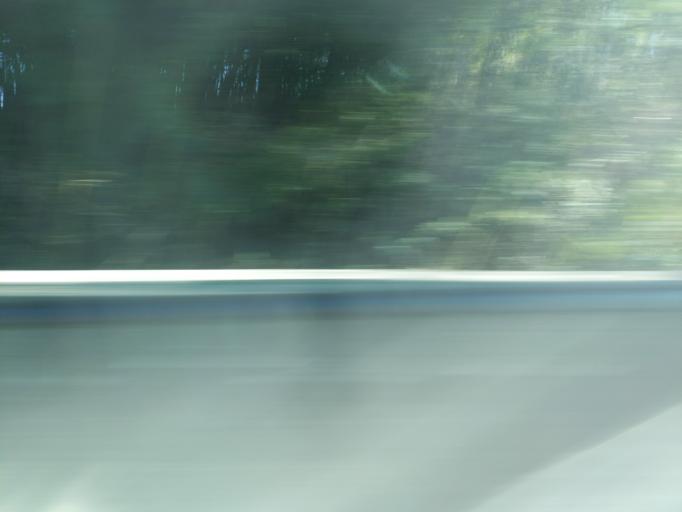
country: JP
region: Fukushima
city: Motomiya
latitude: 37.5285
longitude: 140.4388
